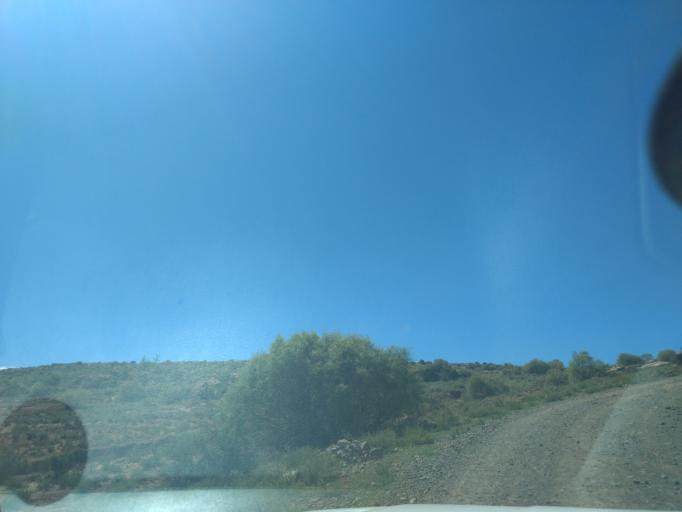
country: LS
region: Maseru
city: Maseru
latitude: -29.4809
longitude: 27.3736
